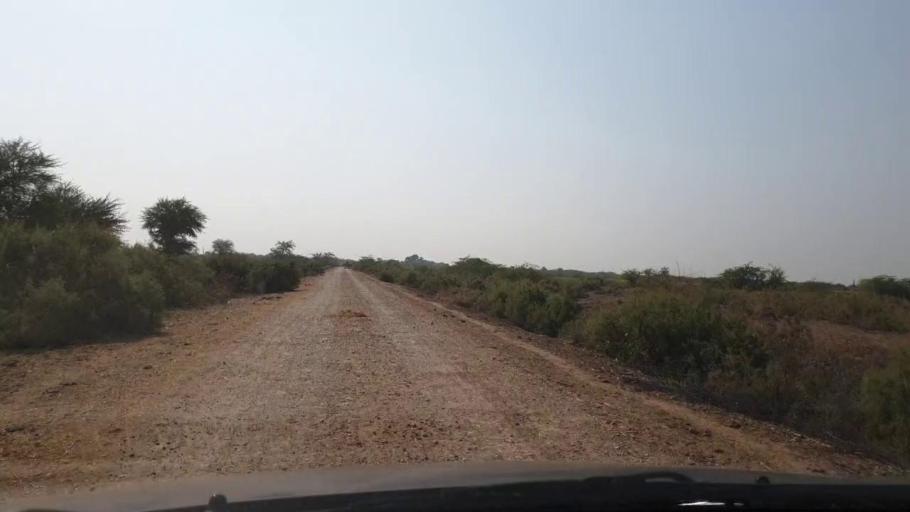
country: PK
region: Sindh
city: Jhol
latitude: 25.8860
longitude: 68.9862
